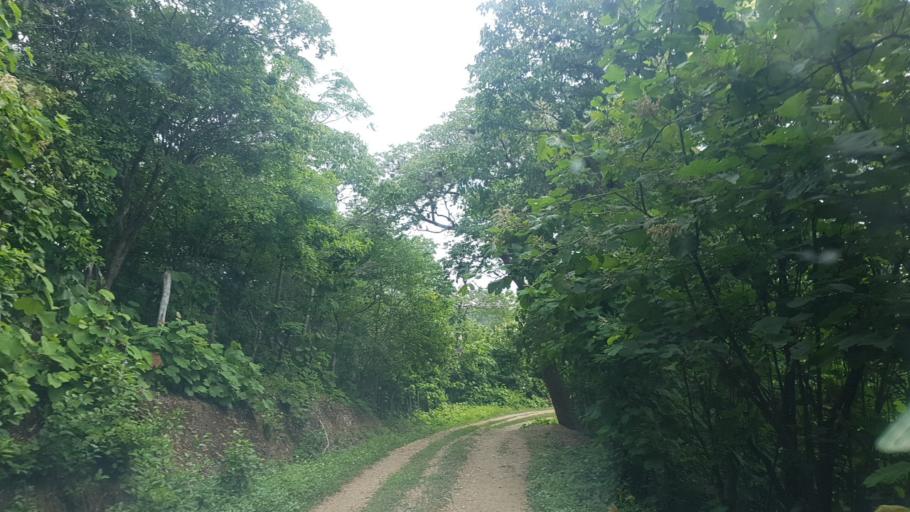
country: NI
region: Nueva Segovia
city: Ciudad Antigua
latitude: 13.6007
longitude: -86.3624
